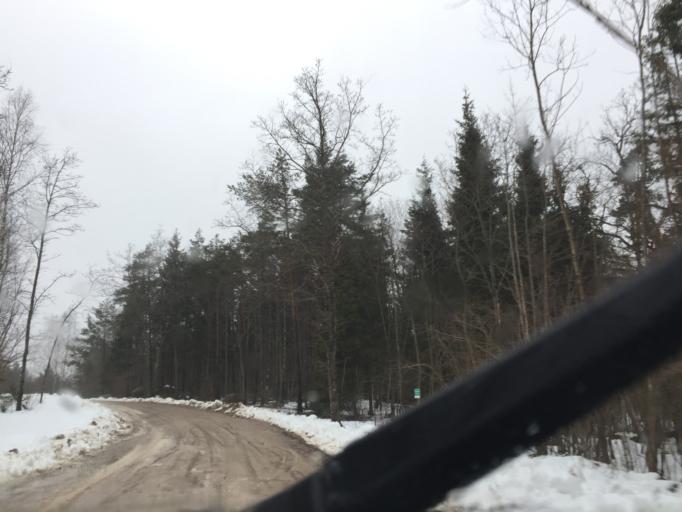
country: EE
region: Saare
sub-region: Kuressaare linn
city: Kuressaare
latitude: 58.2942
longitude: 22.1039
